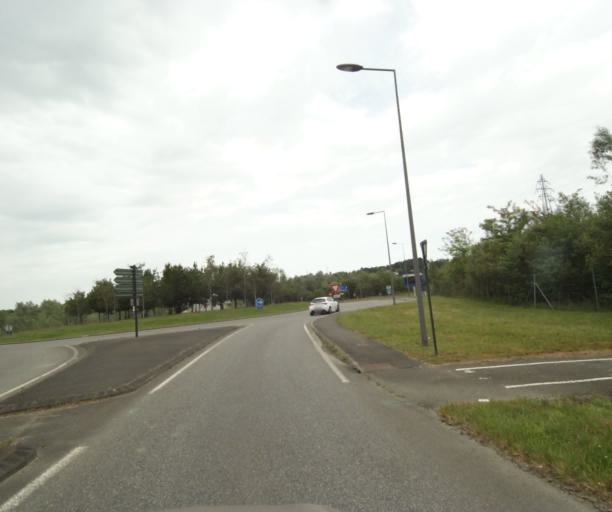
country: FR
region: Aquitaine
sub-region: Departement des Pyrenees-Atlantiques
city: Mouguerre
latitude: 43.4746
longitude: -1.4424
